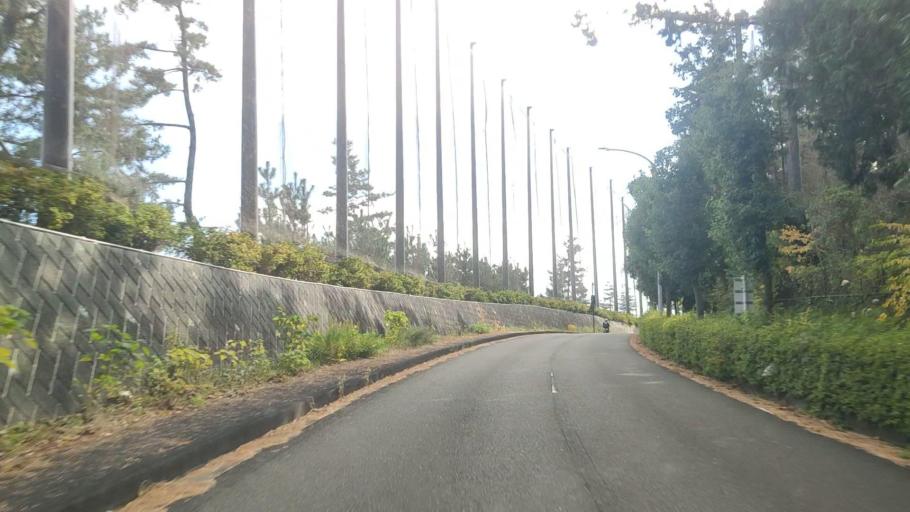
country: JP
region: Kanagawa
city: Yokohama
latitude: 35.4450
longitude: 139.5511
